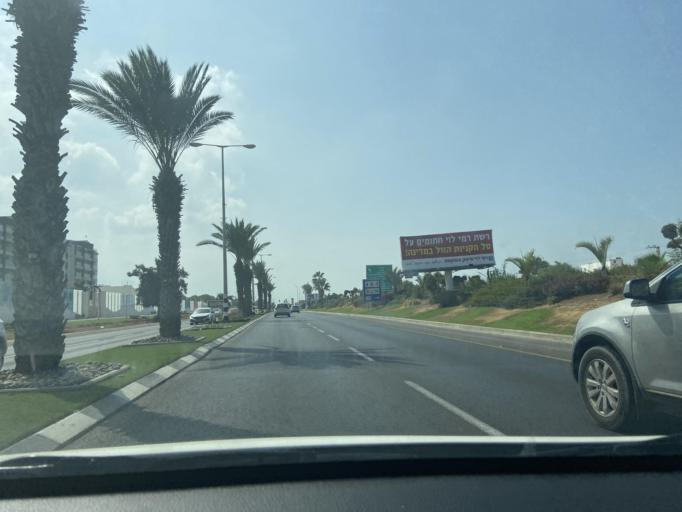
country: IL
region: Northern District
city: Nahariya
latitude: 32.9982
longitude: 35.0979
